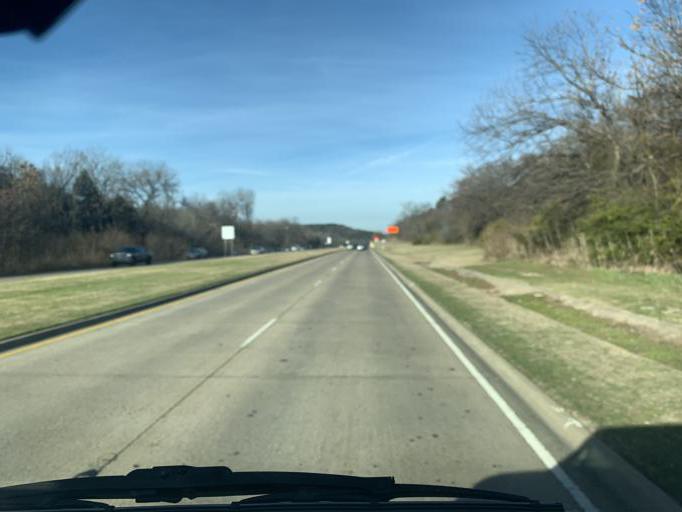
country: US
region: Texas
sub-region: Dallas County
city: Cedar Hill
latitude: 32.6115
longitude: -96.9601
